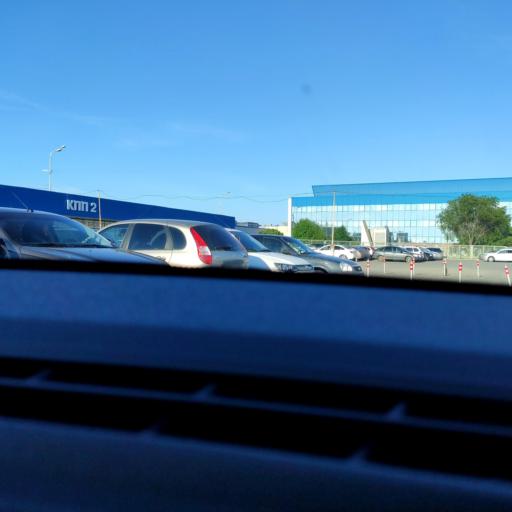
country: RU
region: Samara
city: Tol'yatti
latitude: 53.5565
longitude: 49.2597
